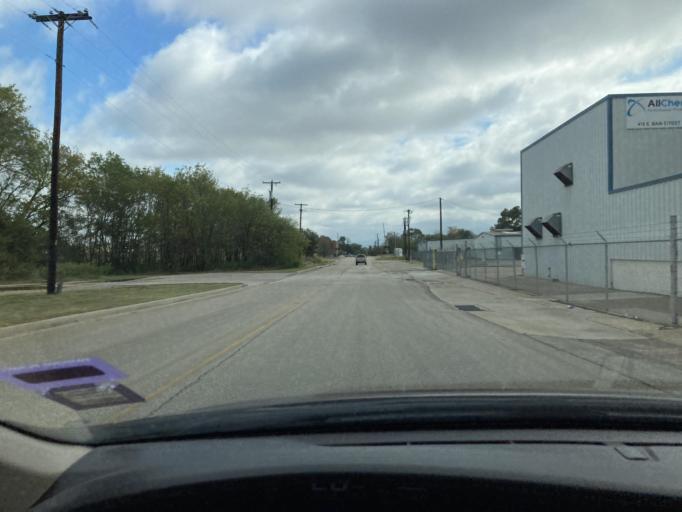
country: US
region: Texas
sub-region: Navarro County
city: Corsicana
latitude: 32.0904
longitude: -96.4630
